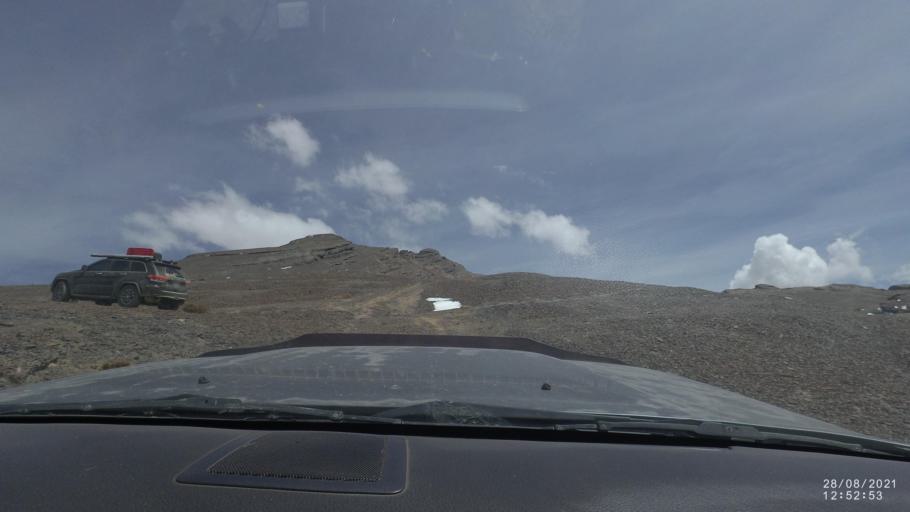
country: BO
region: Cochabamba
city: Sipe Sipe
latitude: -17.2825
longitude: -66.3843
